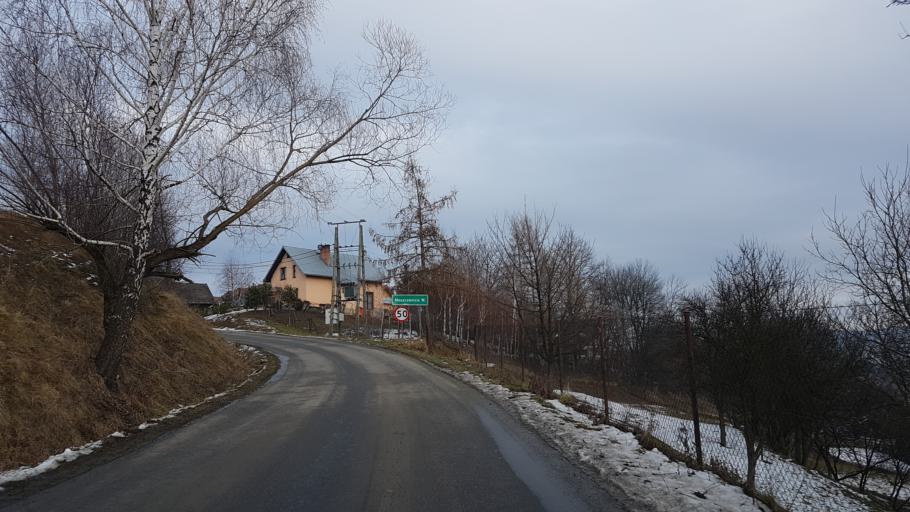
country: PL
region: Lesser Poland Voivodeship
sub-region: Powiat nowosadecki
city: Stary Sacz
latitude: 49.5118
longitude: 20.5982
